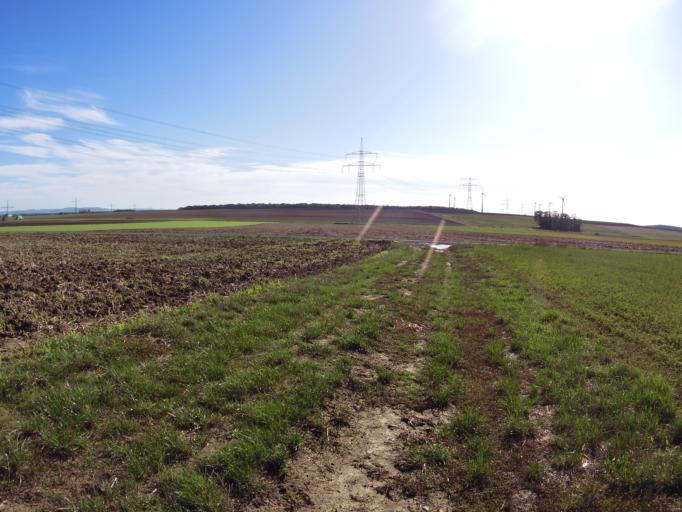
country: DE
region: Bavaria
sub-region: Regierungsbezirk Unterfranken
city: Theilheim
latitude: 49.7460
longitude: 10.0504
